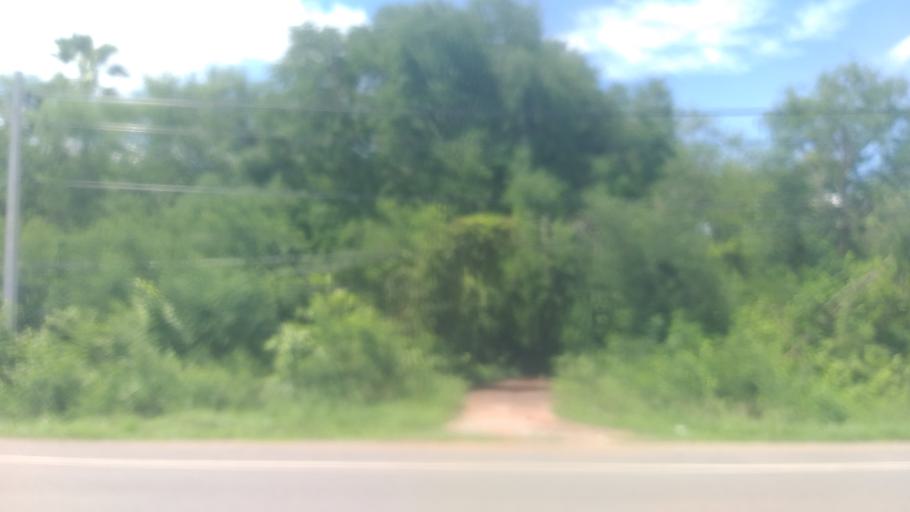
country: TH
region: Nakhon Ratchasima
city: Phra Thong Kham
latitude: 15.2944
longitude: 101.9881
